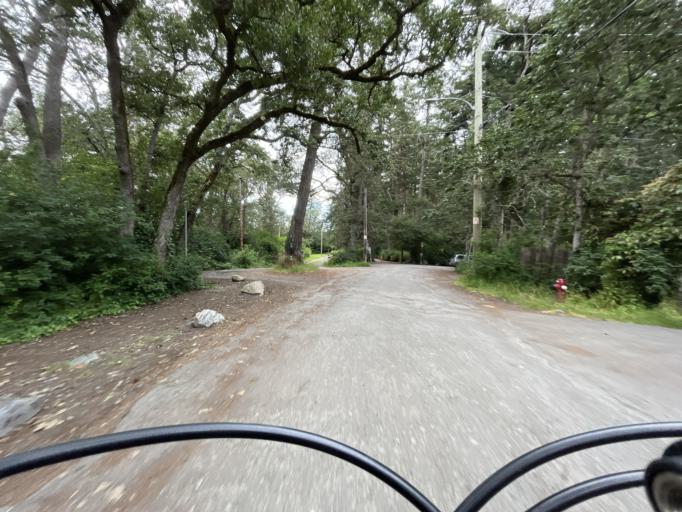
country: CA
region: British Columbia
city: Oak Bay
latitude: 48.4820
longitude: -123.3461
